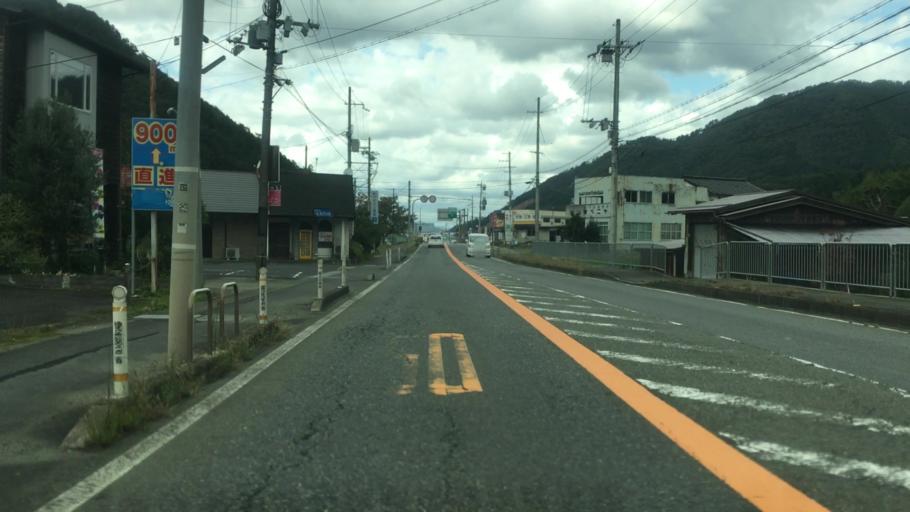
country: JP
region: Hyogo
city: Toyooka
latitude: 35.3195
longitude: 134.8816
